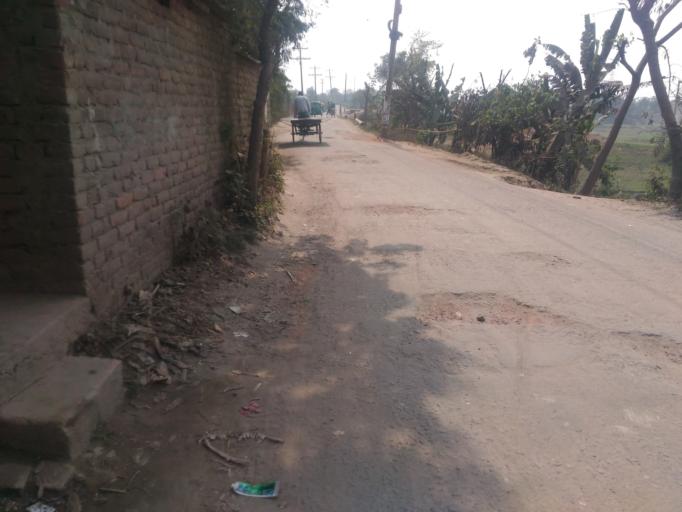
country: BD
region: Dhaka
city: Narayanganj
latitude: 23.6533
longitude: 90.4473
